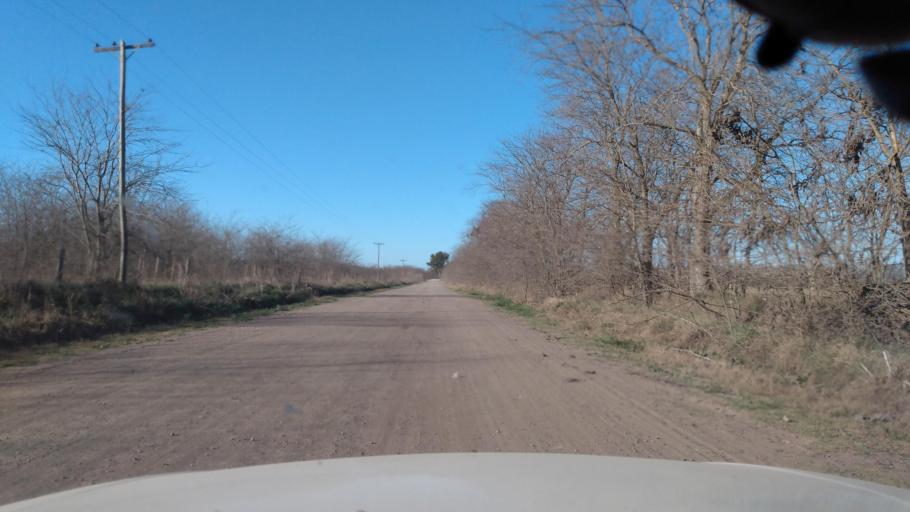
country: AR
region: Buenos Aires
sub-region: Partido de Mercedes
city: Mercedes
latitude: -34.6146
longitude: -59.3307
